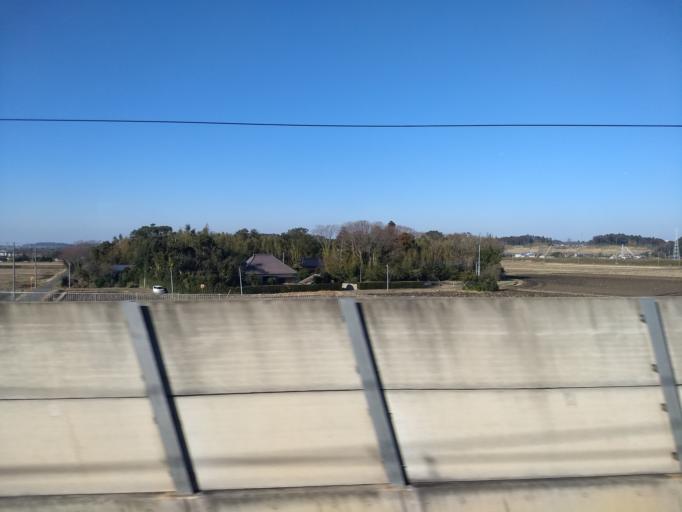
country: JP
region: Chiba
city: Narita
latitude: 35.7989
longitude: 140.2811
